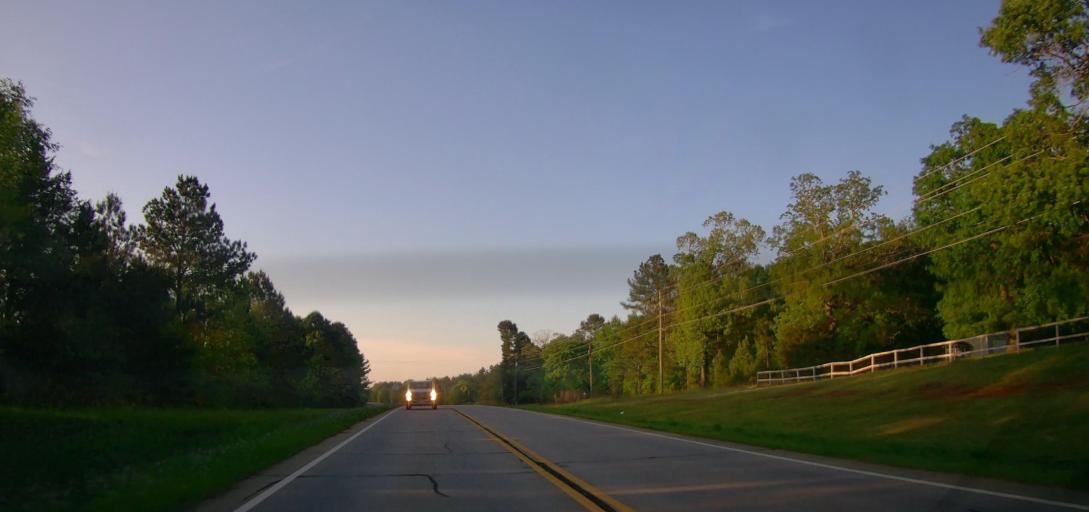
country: US
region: Georgia
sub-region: Newton County
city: Oakwood
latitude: 33.5089
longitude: -83.9479
